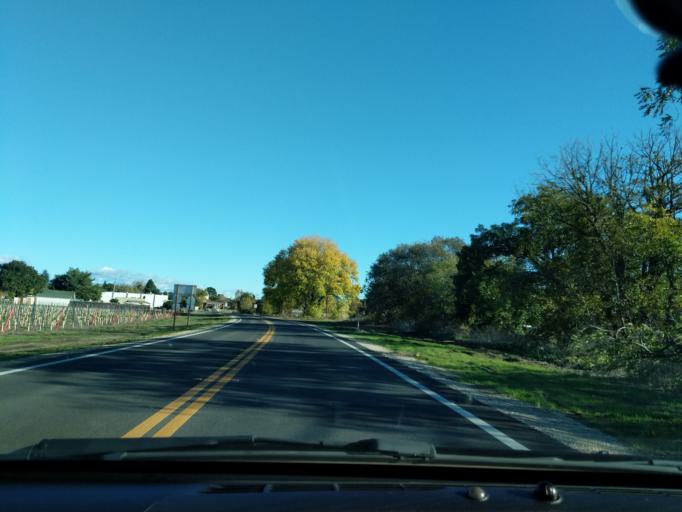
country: US
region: California
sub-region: Santa Barbara County
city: Los Alamos
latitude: 34.7449
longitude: -120.2858
